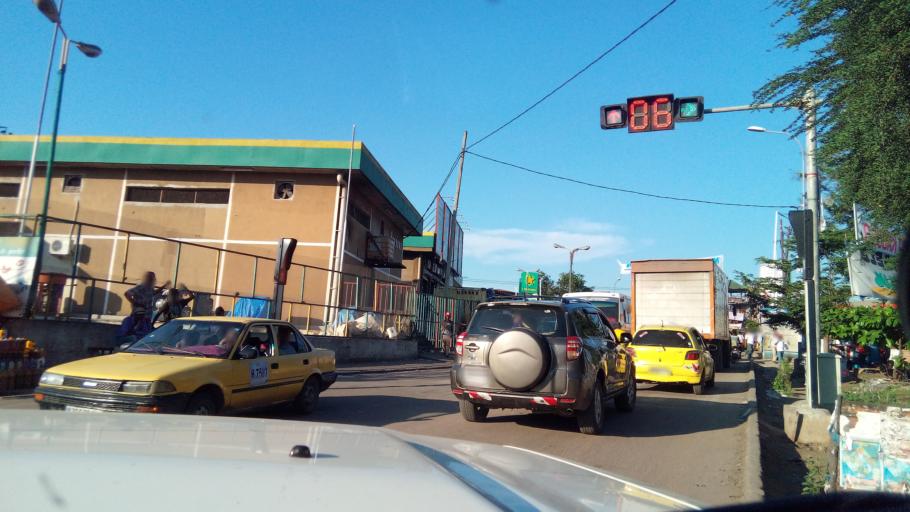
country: CD
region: Kinshasa
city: Kinshasa
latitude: -4.3469
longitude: 15.2636
